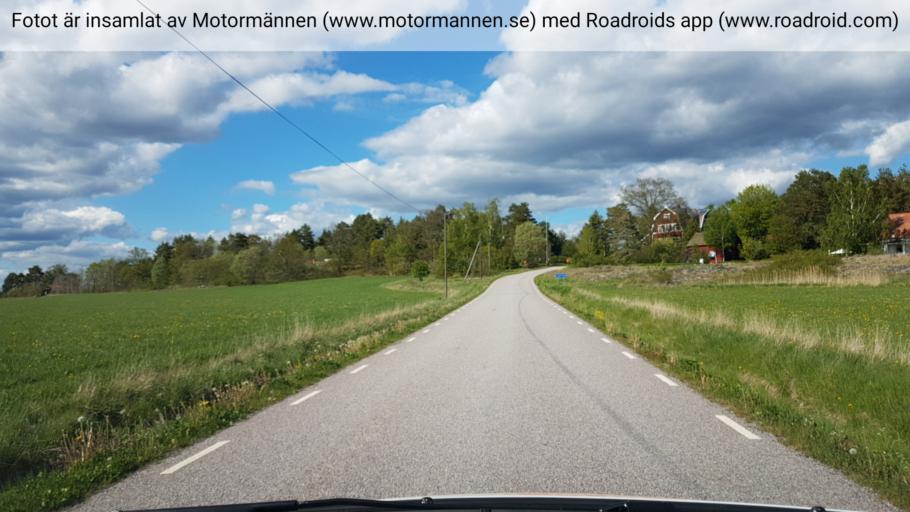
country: SE
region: Kalmar
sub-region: Vasterviks Kommun
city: Forserum
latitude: 57.9355
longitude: 16.4598
